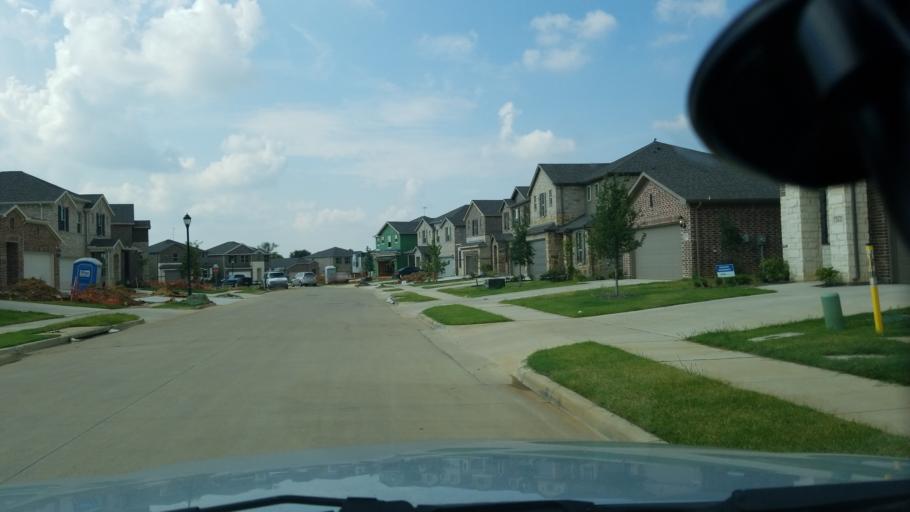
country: US
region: Texas
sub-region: Dallas County
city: Irving
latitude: 32.8428
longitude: -96.9196
